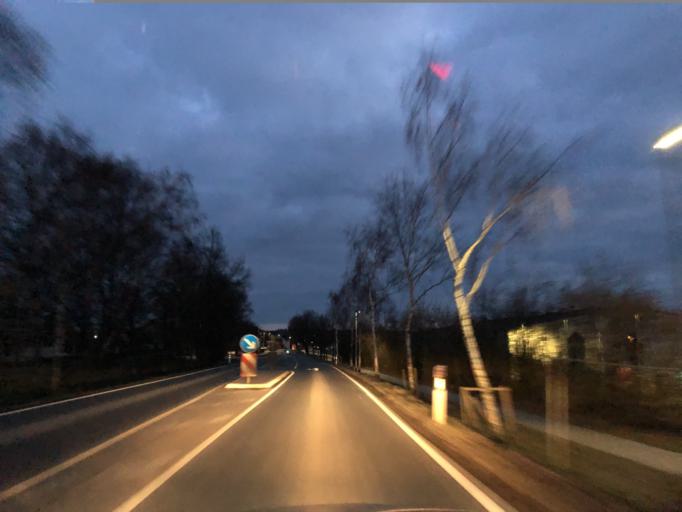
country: DE
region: Rheinland-Pfalz
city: Singhofen
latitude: 50.2804
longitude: 7.8337
